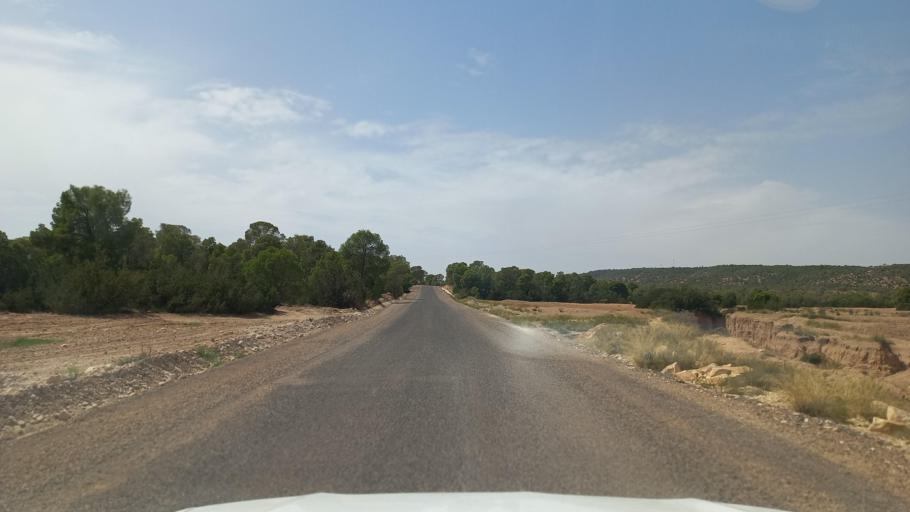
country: TN
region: Al Qasrayn
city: Sbiba
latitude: 35.3837
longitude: 8.9350
